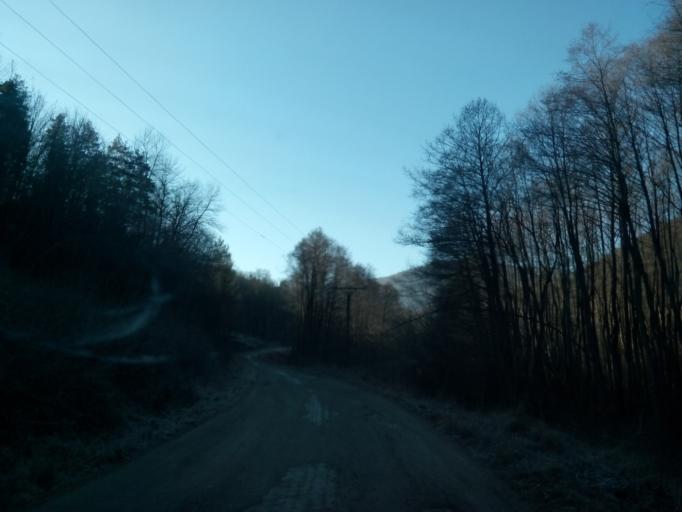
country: SK
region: Kosicky
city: Medzev
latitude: 48.6828
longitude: 20.8897
